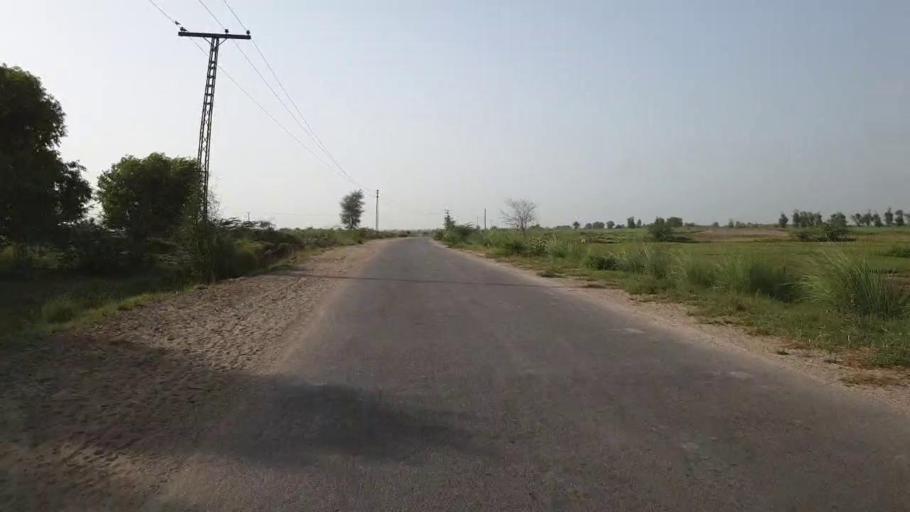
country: PK
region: Sindh
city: Jam Sahib
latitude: 26.3943
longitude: 68.8794
